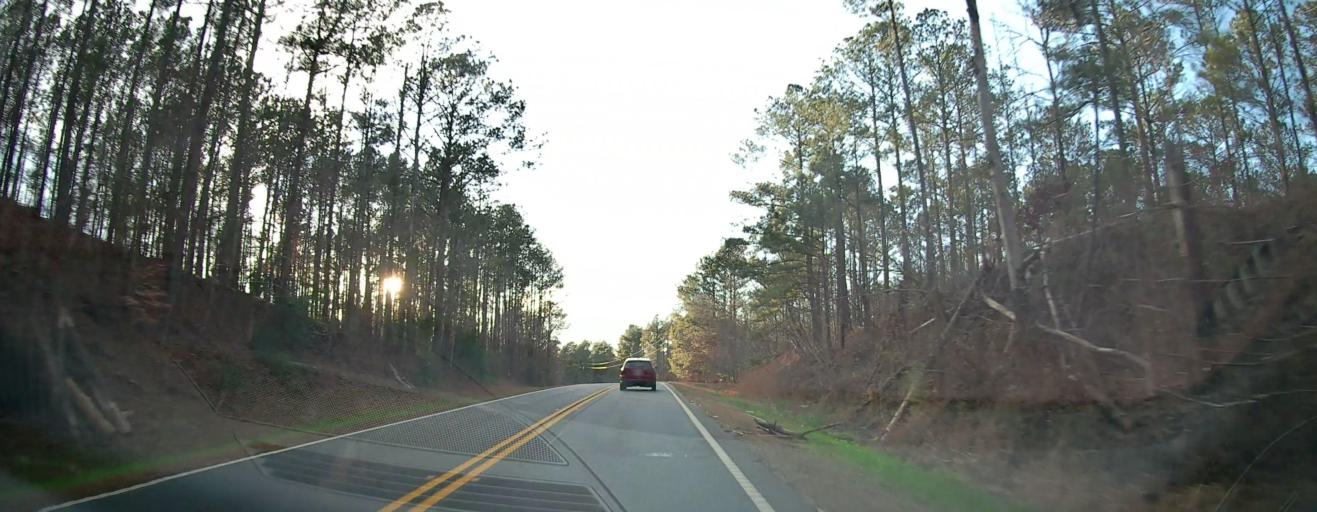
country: US
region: Georgia
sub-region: Talbot County
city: Sardis
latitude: 32.7231
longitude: -84.6430
